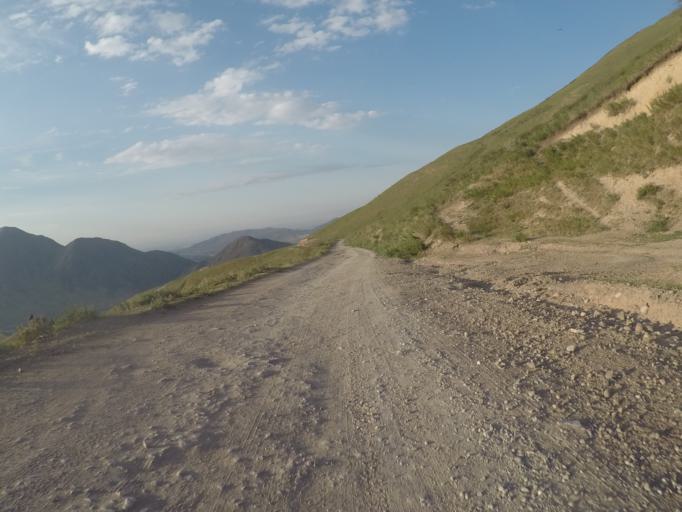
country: KG
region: Chuy
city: Bishkek
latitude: 42.6516
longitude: 74.6615
